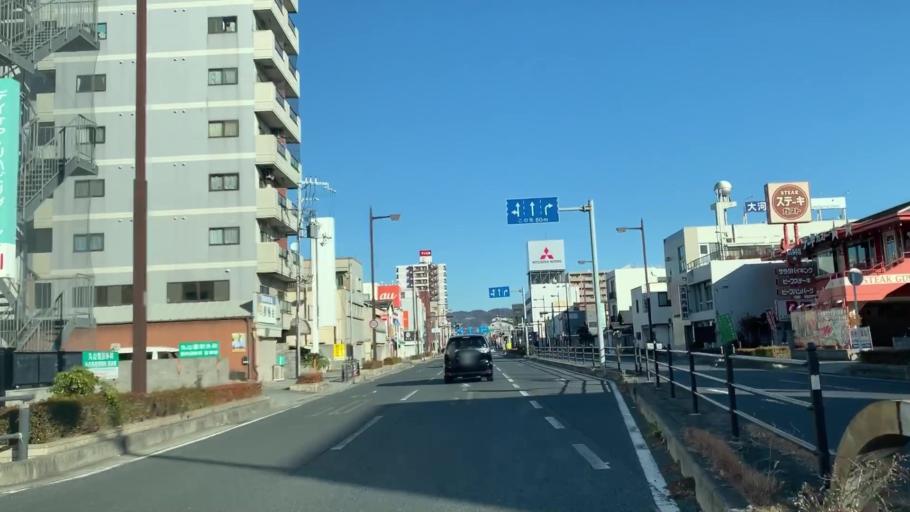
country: JP
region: Wakayama
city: Wakayama-shi
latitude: 34.2344
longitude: 135.1695
